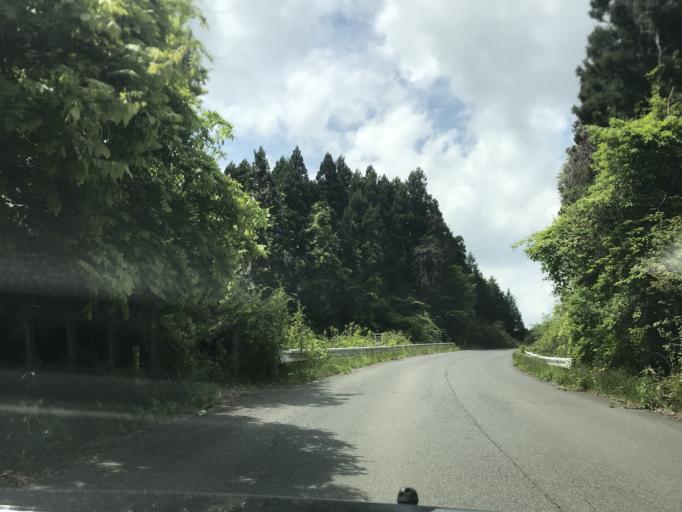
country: JP
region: Miyagi
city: Furukawa
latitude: 38.7207
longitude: 140.9224
